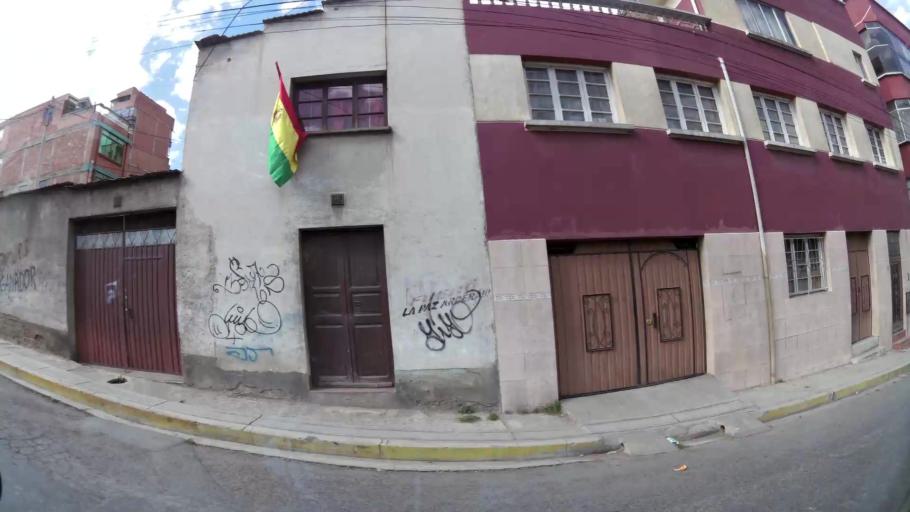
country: BO
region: La Paz
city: La Paz
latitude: -16.4747
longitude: -68.1515
